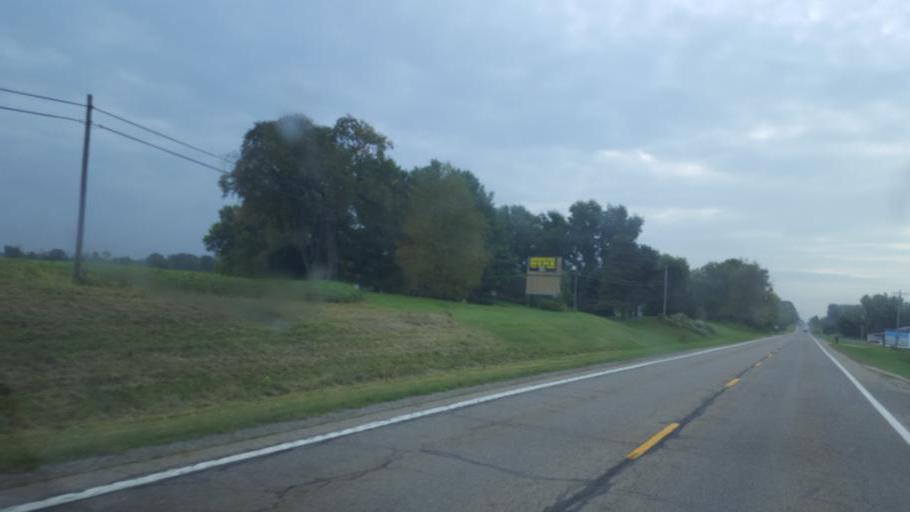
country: US
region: Ohio
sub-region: Morrow County
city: Mount Gilead
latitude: 40.5243
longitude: -82.7550
